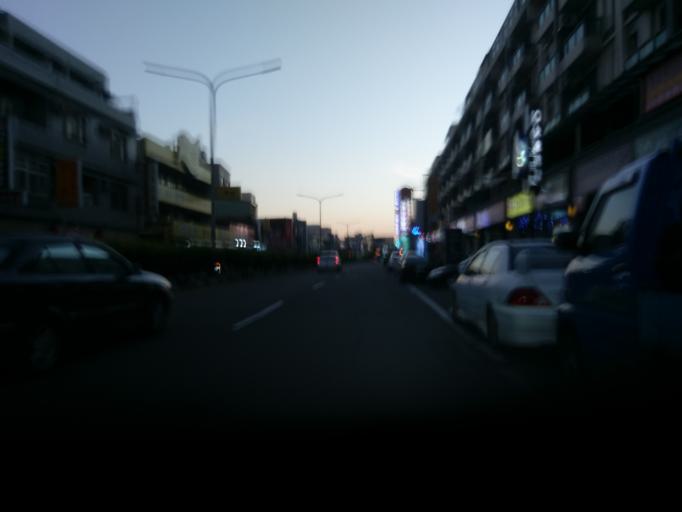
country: TW
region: Taiwan
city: Taoyuan City
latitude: 25.0449
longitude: 121.1398
